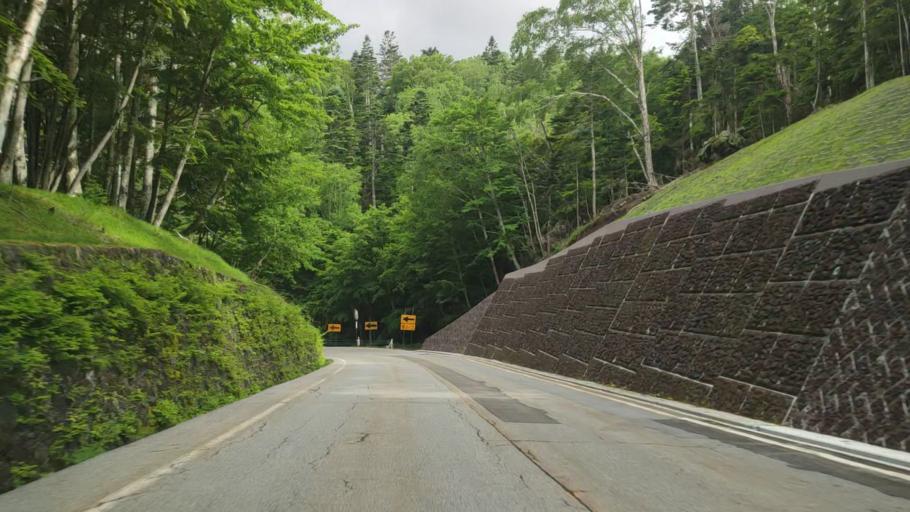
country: JP
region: Yamanashi
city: Fujikawaguchiko
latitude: 35.4154
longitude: 138.7134
